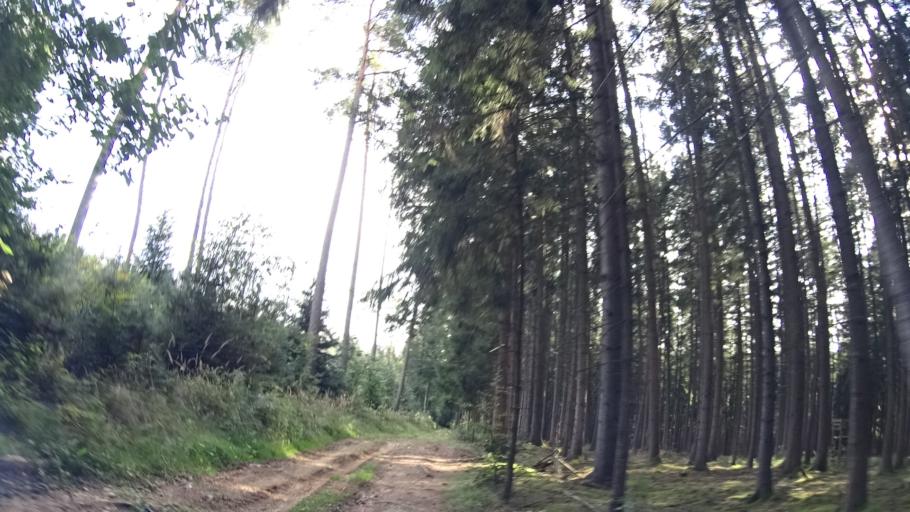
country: DE
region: Bavaria
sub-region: Upper Bavaria
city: Mindelstetten
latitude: 48.9150
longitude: 11.6397
